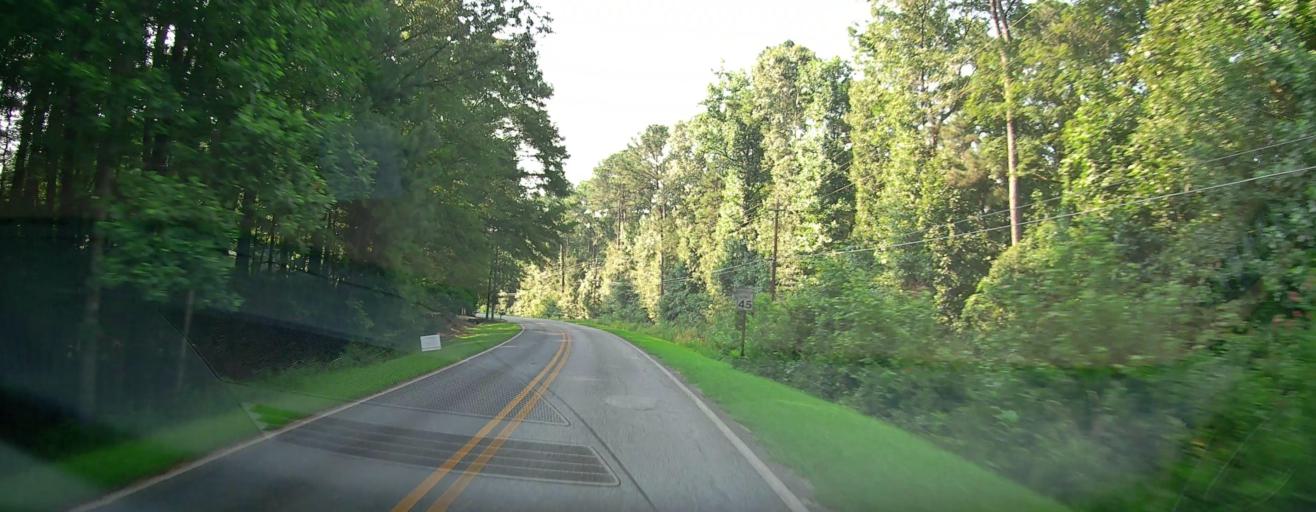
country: US
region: Georgia
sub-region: Bibb County
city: Macon
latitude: 32.9540
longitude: -83.7318
